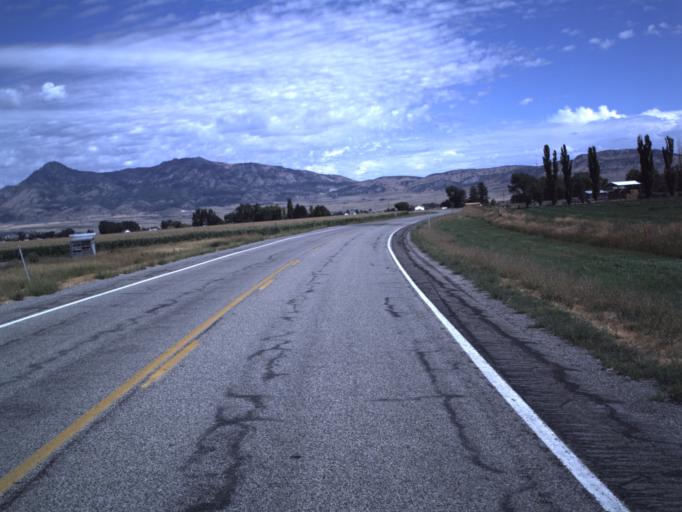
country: US
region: Utah
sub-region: Box Elder County
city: Garland
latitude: 41.7948
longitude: -112.1486
